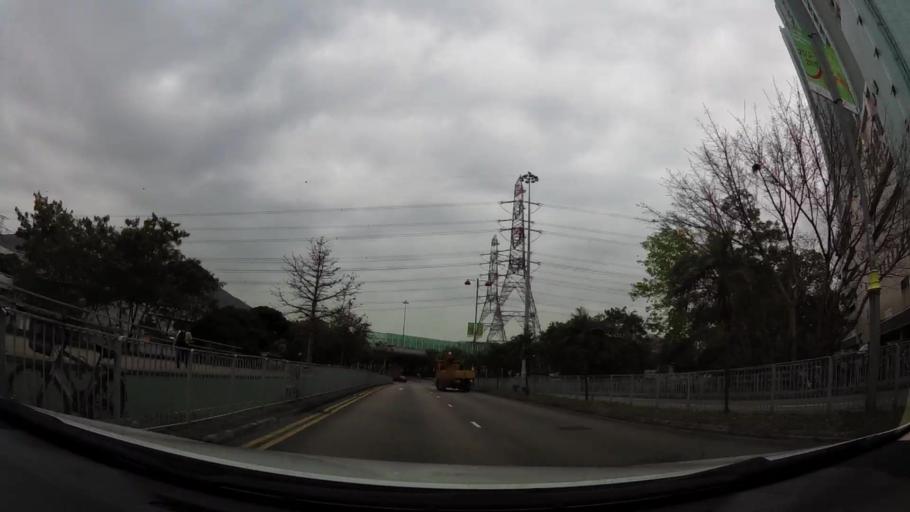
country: HK
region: Tuen Mun
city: Tuen Mun
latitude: 22.4139
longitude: 113.9823
